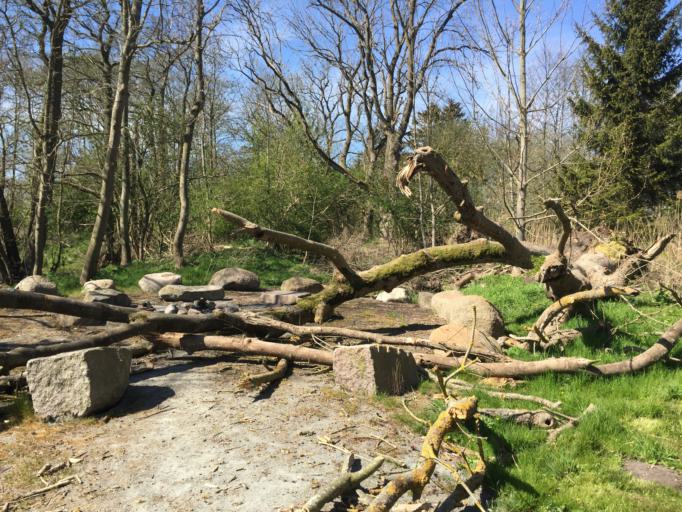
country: DK
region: South Denmark
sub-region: Odense Kommune
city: Hojby
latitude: 55.3454
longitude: 10.4154
